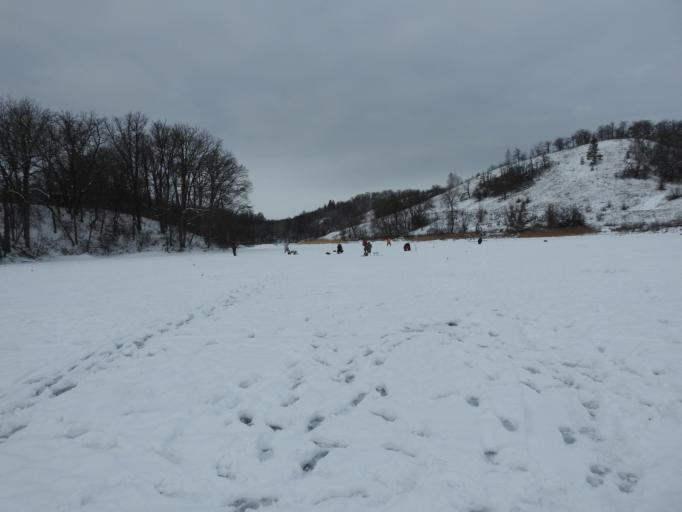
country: RU
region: Saratov
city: Tersa
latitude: 52.1048
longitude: 47.4800
